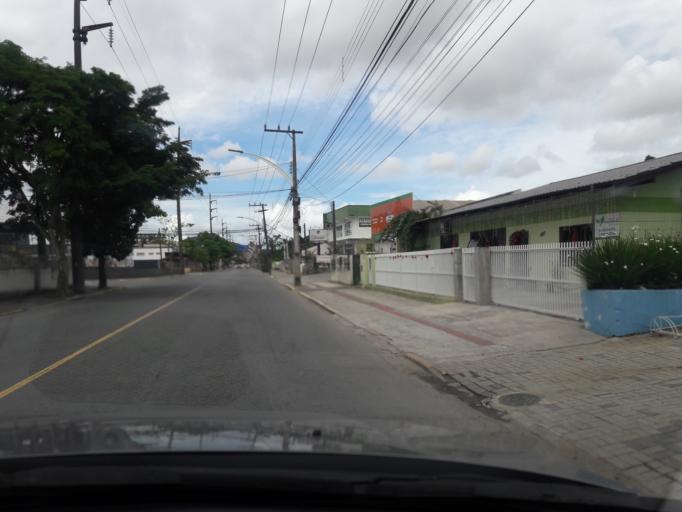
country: BR
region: Santa Catarina
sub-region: Joinville
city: Joinville
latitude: -26.3239
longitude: -48.8550
